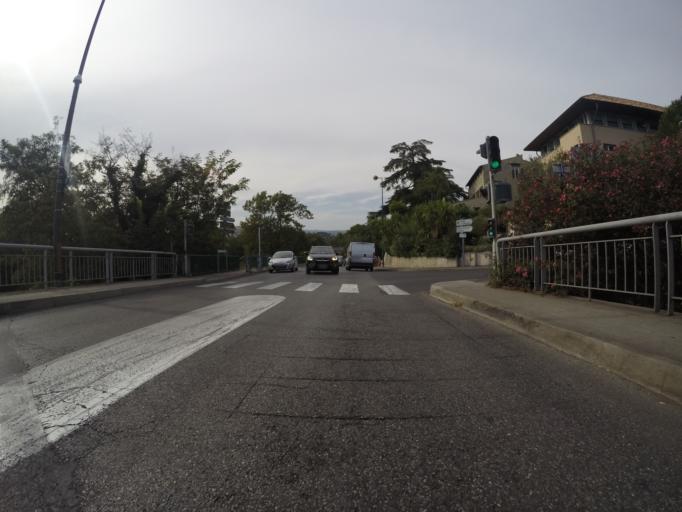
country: FR
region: Provence-Alpes-Cote d'Azur
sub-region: Departement des Alpes-Maritimes
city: Cagnes-sur-Mer
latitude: 43.6609
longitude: 7.1550
